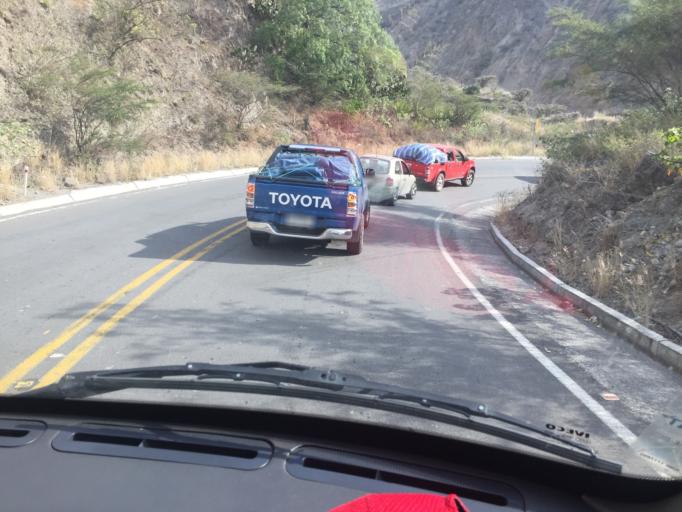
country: EC
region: Carchi
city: El Angel
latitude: 0.6037
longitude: -78.1371
